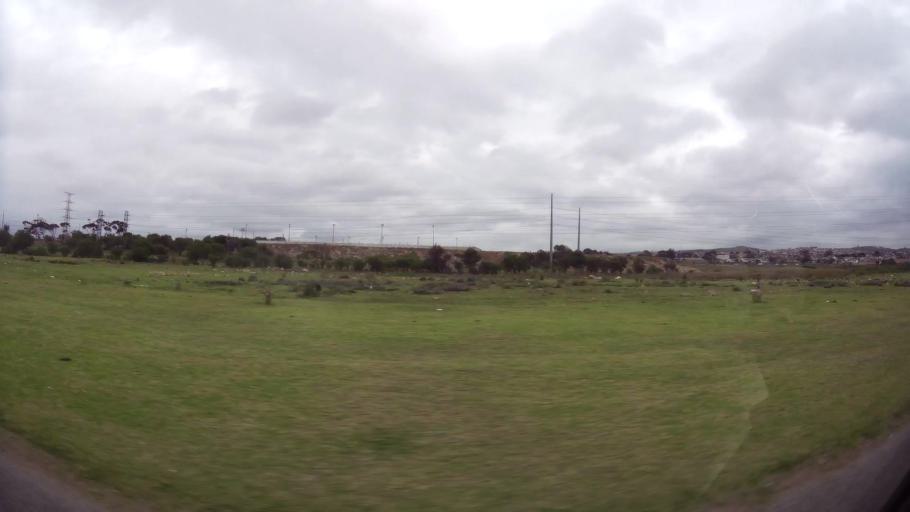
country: ZA
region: Eastern Cape
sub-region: Nelson Mandela Bay Metropolitan Municipality
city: Port Elizabeth
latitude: -33.9072
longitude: 25.5611
